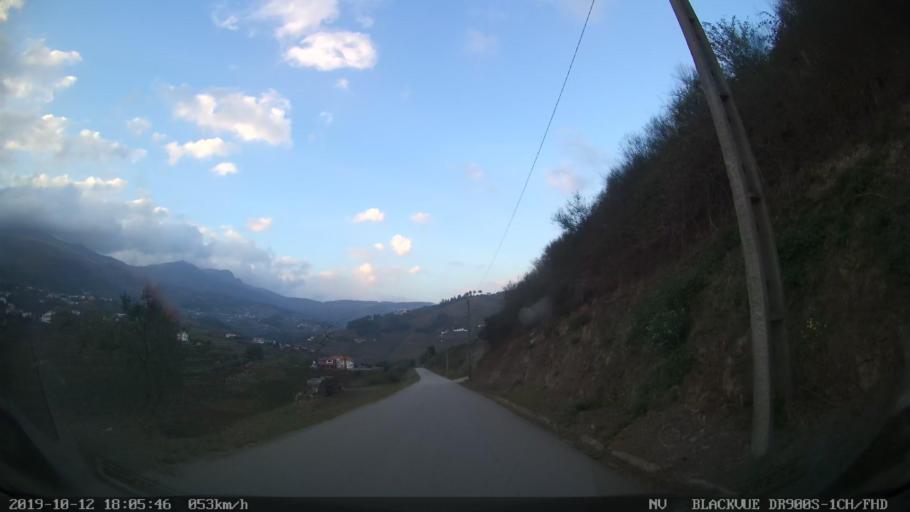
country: PT
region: Vila Real
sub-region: Mesao Frio
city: Mesao Frio
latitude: 41.1789
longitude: -7.8452
